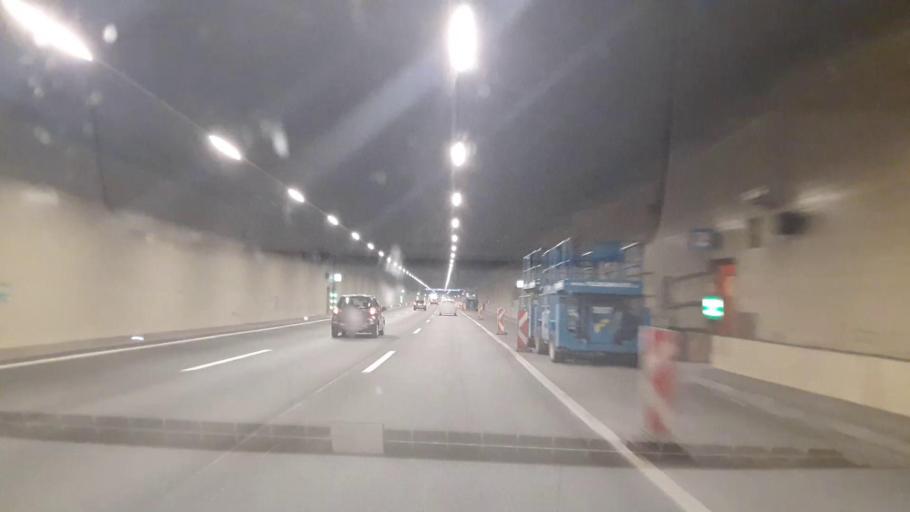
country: AT
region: Vienna
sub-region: Wien Stadt
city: Vienna
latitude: 48.2291
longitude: 16.4147
